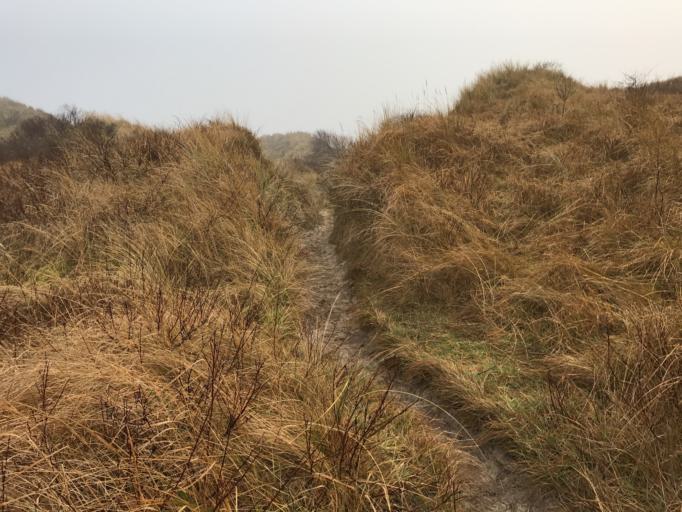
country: DE
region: Lower Saxony
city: Borkum
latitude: 53.6078
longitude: 6.7331
